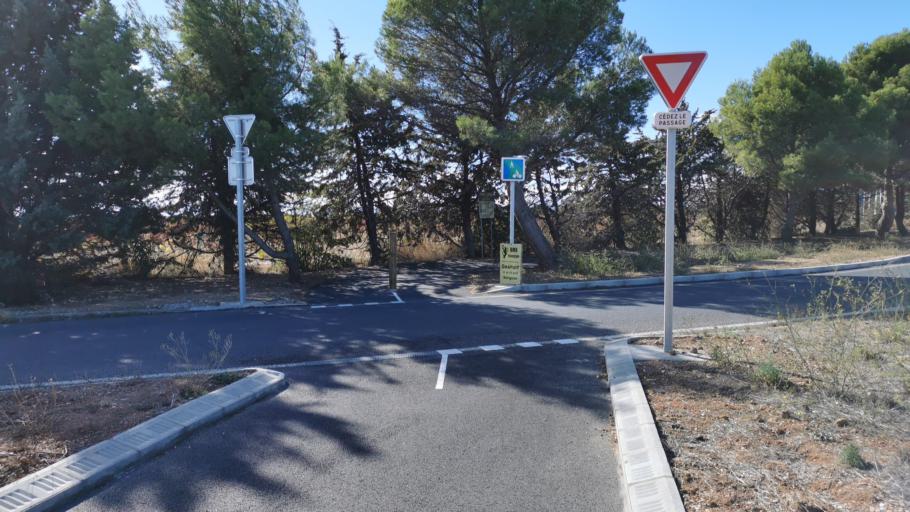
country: FR
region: Languedoc-Roussillon
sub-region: Departement de l'Herault
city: Valras-Plage
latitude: 43.2397
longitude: 3.2543
